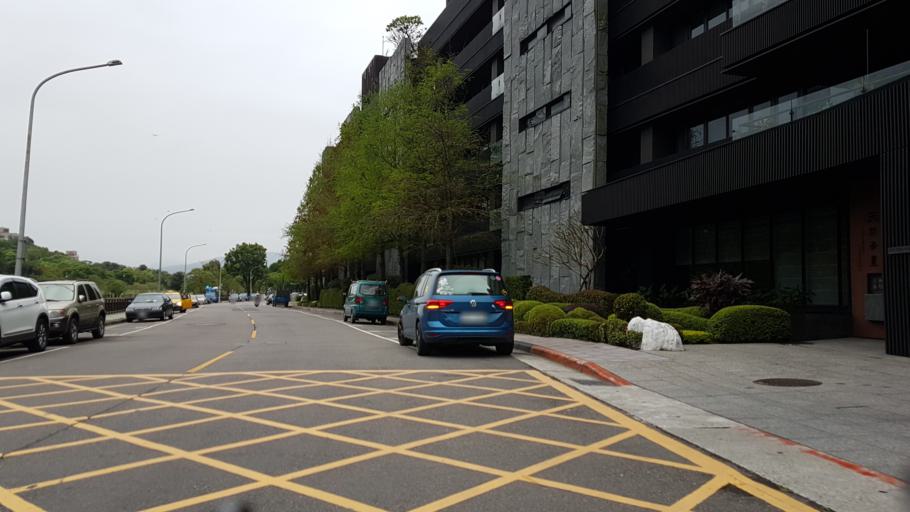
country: TW
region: Taipei
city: Taipei
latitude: 25.0414
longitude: 121.5932
